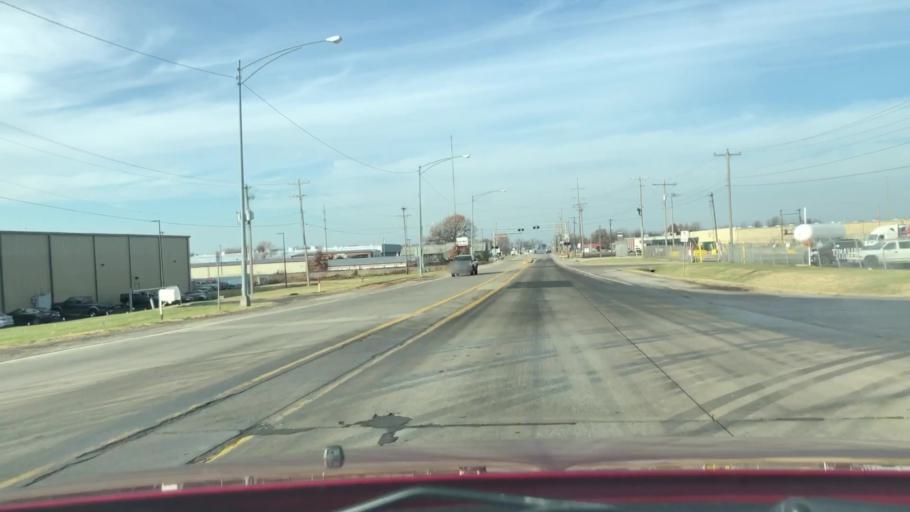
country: US
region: Missouri
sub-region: Greene County
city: Springfield
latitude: 37.2244
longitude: -93.2280
